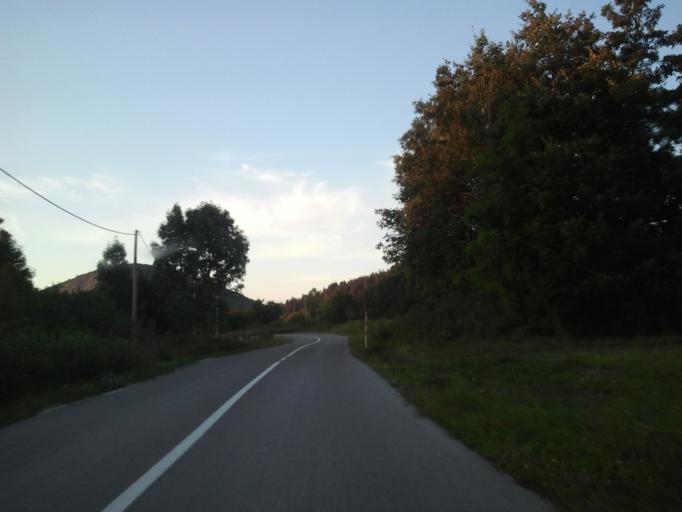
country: HR
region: Zadarska
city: Obrovac
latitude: 44.4211
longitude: 15.6600
